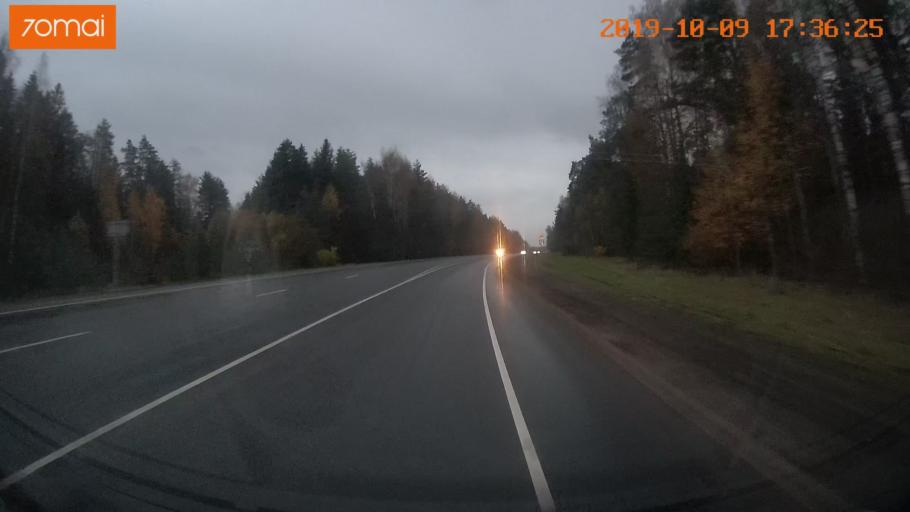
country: RU
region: Ivanovo
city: Bogorodskoye
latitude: 57.0786
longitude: 40.9974
